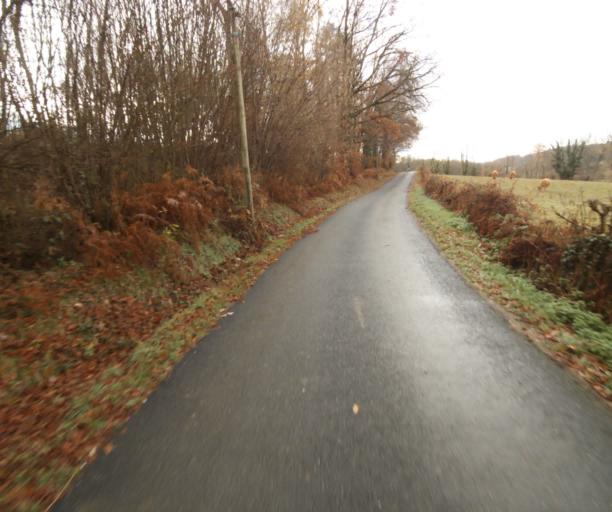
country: FR
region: Limousin
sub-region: Departement de la Correze
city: Saint-Mexant
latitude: 45.2531
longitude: 1.6451
